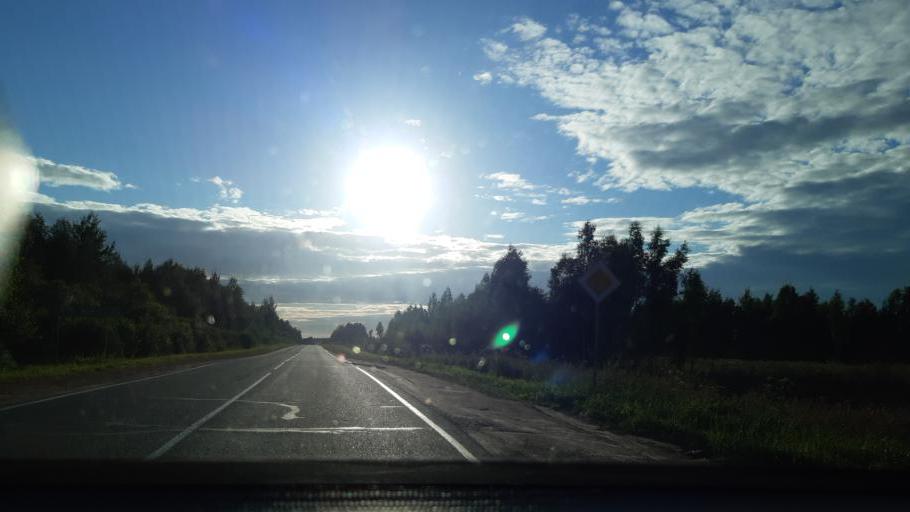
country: RU
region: Smolensk
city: Yel'nya
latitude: 54.5582
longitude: 33.1840
